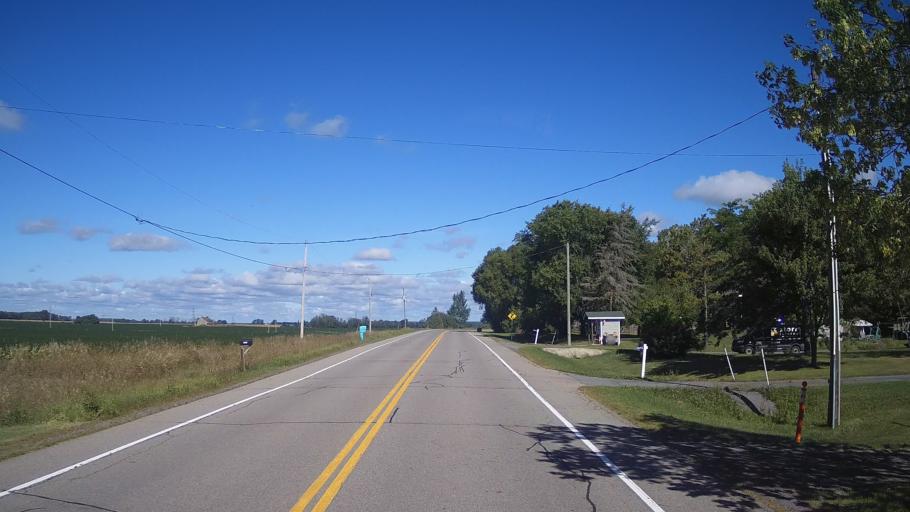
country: US
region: New York
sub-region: St. Lawrence County
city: Norfolk
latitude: 44.9562
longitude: -75.2812
